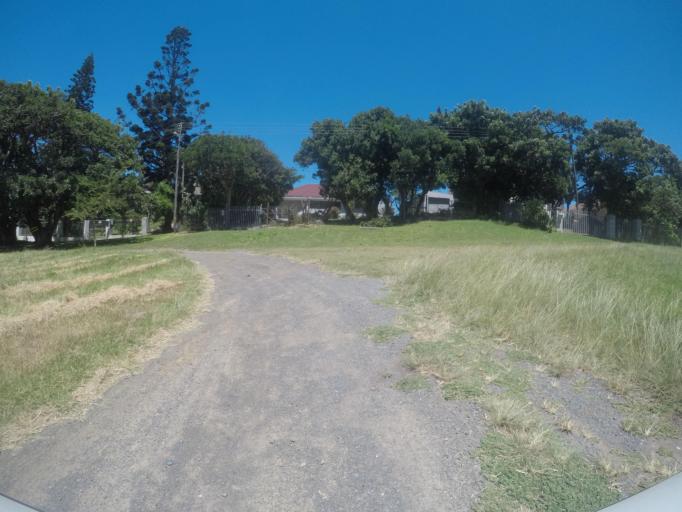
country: ZA
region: Eastern Cape
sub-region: Buffalo City Metropolitan Municipality
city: East London
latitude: -32.9573
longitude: 27.9967
